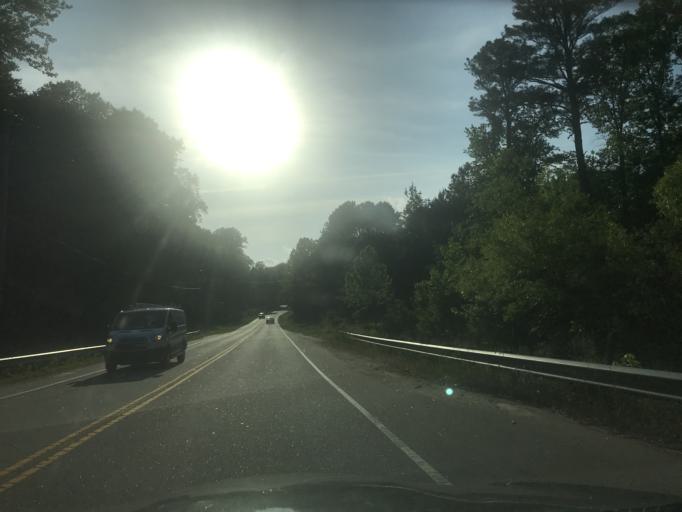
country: US
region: North Carolina
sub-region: Wake County
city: Knightdale
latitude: 35.7542
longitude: -78.5087
